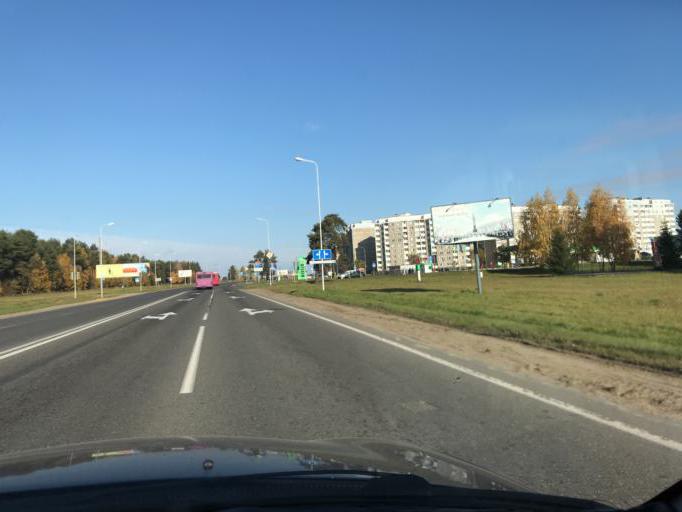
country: BY
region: Grodnenskaya
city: Lida
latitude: 53.8906
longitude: 25.2526
